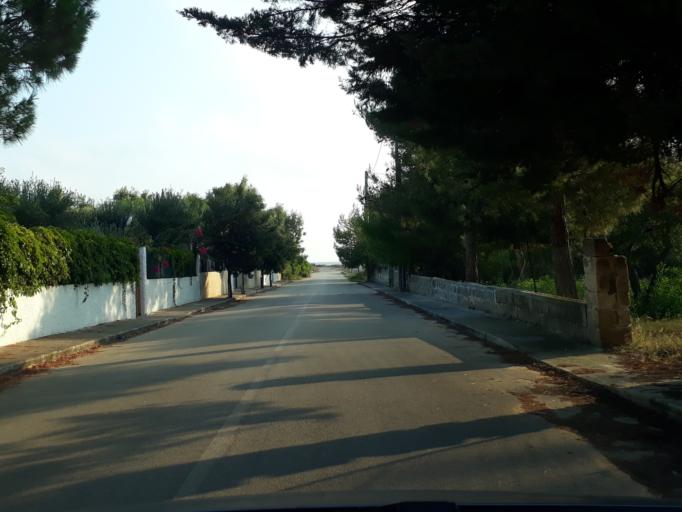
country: IT
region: Apulia
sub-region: Provincia di Brindisi
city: Carovigno
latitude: 40.7505
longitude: 17.7160
